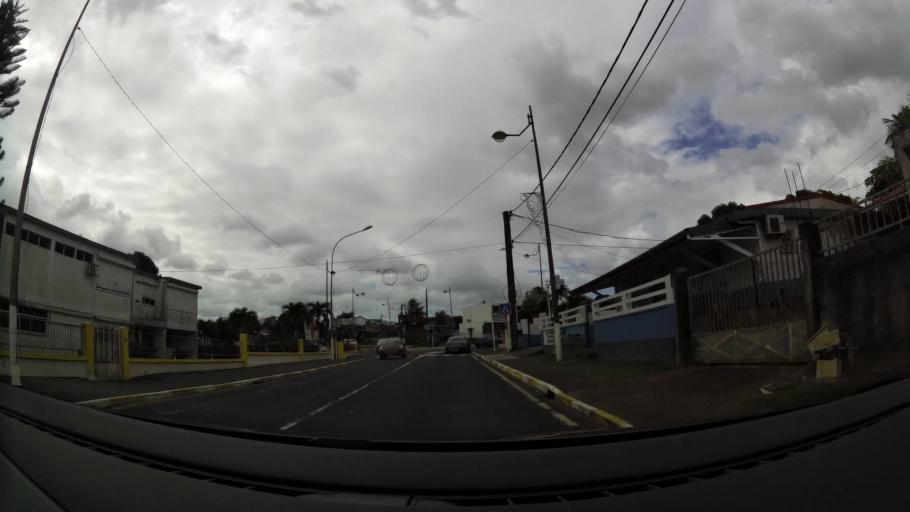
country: GP
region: Guadeloupe
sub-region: Guadeloupe
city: Lamentin
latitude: 16.2713
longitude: -61.6355
